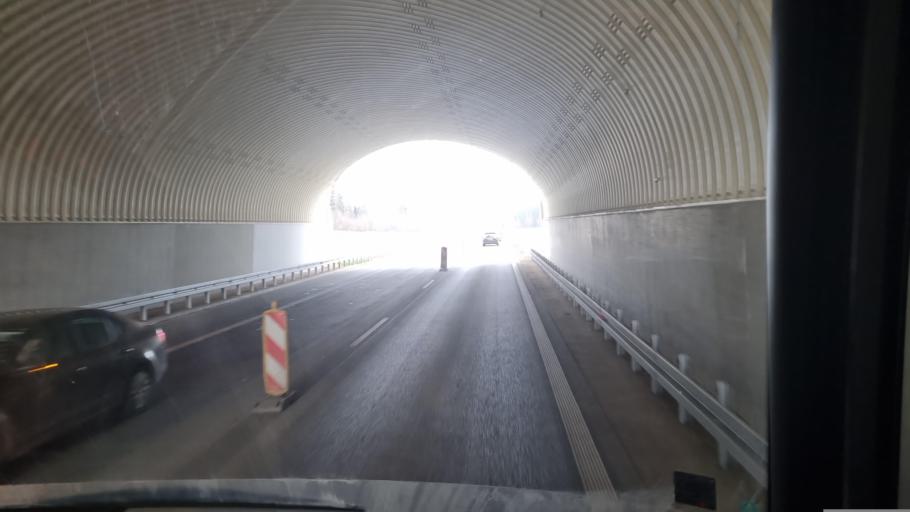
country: PL
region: Warmian-Masurian Voivodeship
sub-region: Powiat elcki
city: Elk
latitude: 53.8414
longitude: 22.4425
